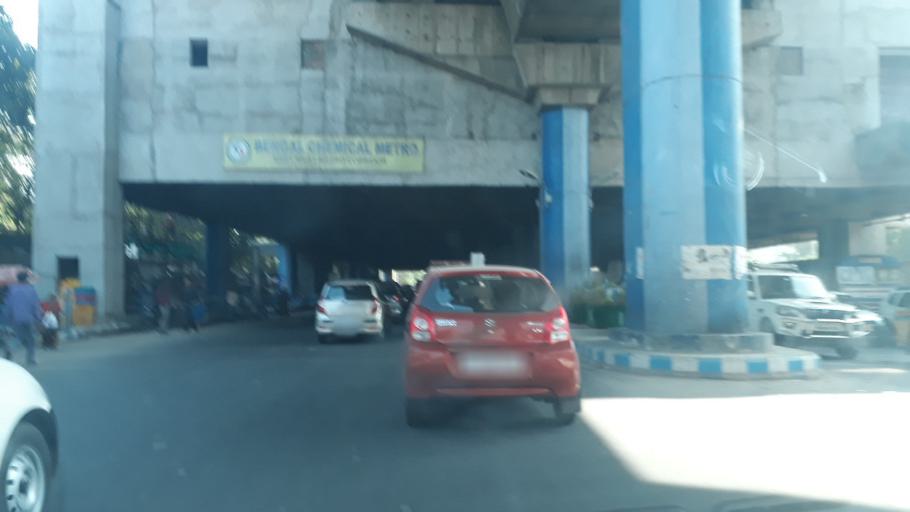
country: IN
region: West Bengal
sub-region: Kolkata
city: Kolkata
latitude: 22.5808
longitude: 88.4012
